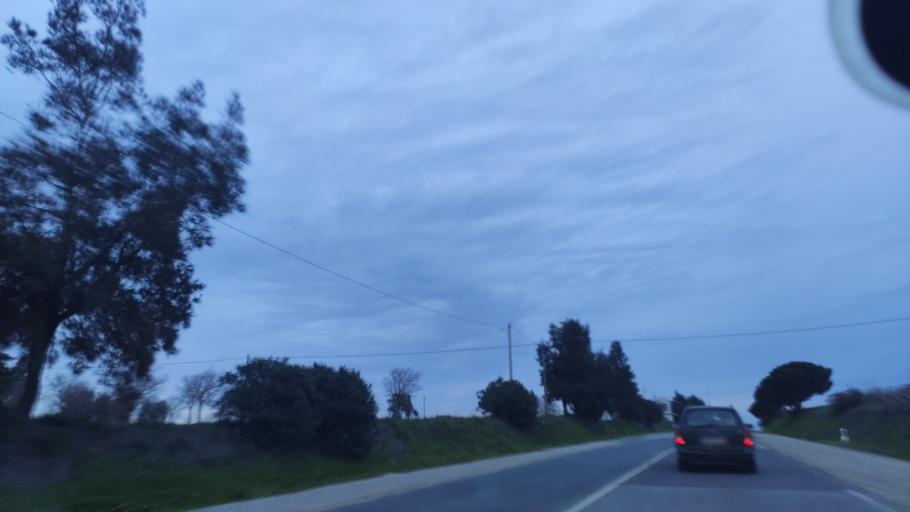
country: PT
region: Beja
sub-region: Beja
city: Beja
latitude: 38.0262
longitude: -7.8700
